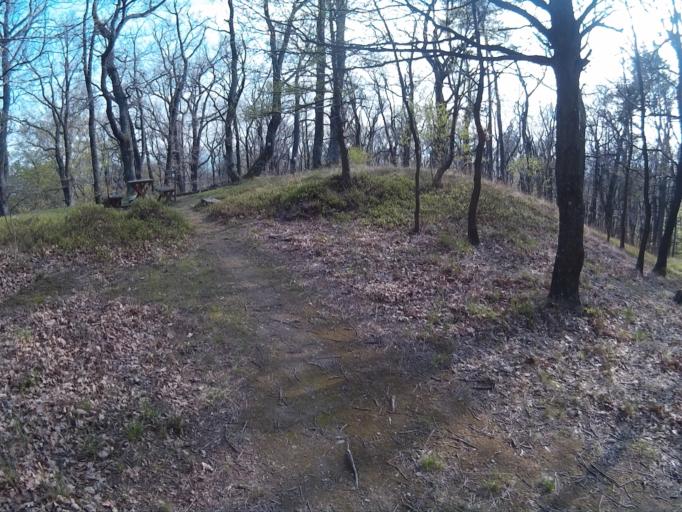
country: AT
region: Burgenland
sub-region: Politischer Bezirk Oberwart
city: Rechnitz
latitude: 47.3323
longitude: 16.4664
